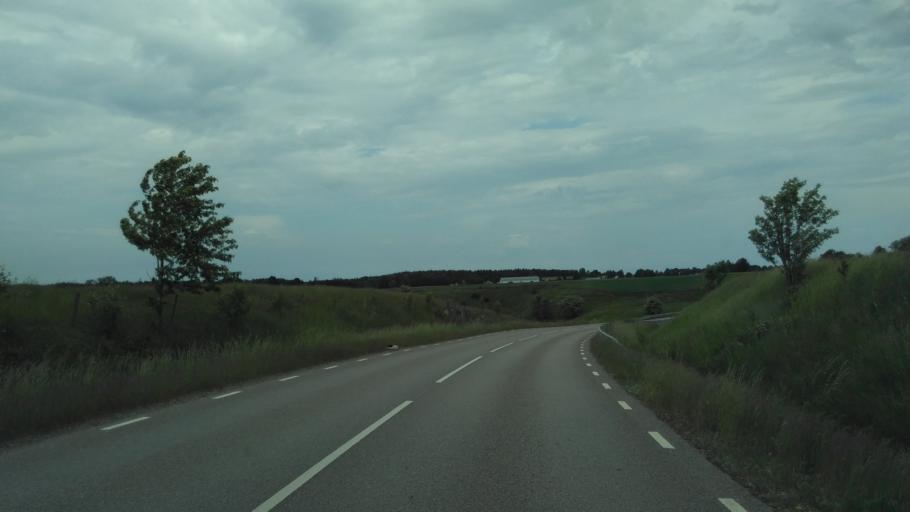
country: SE
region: Vaestra Goetaland
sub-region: Lidkopings Kommun
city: Lidkoping
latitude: 58.4216
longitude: 13.1584
